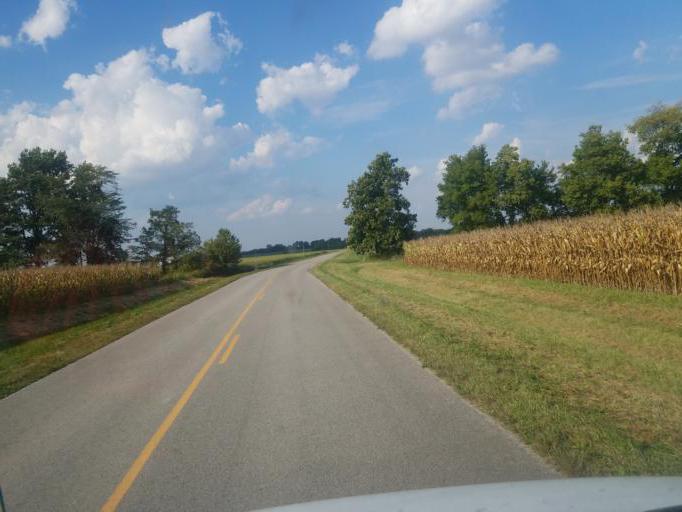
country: US
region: Ohio
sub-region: Hancock County
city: Arlington
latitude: 40.8870
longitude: -83.5684
